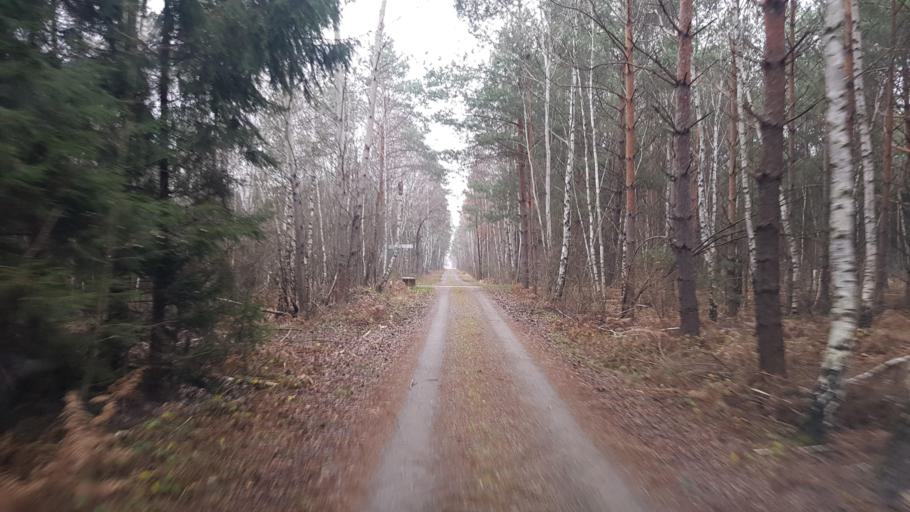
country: DE
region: Brandenburg
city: Plessa
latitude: 51.5205
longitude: 13.6284
